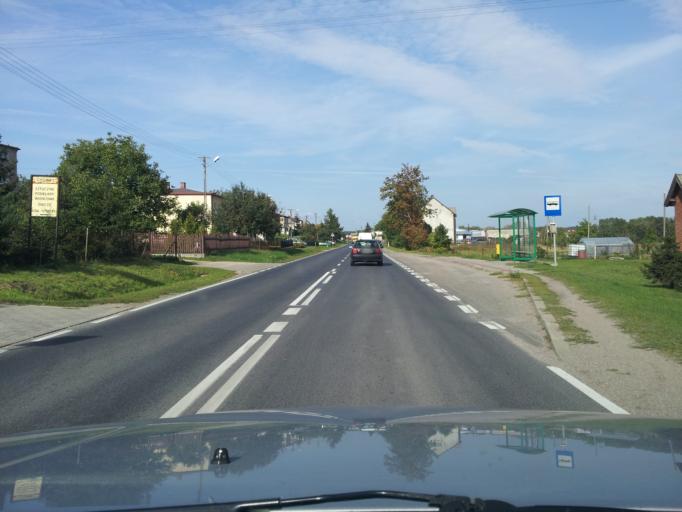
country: PL
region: Warmian-Masurian Voivodeship
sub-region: Powiat nowomiejski
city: Nowe Miasto Lubawskie
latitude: 53.4523
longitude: 19.6020
